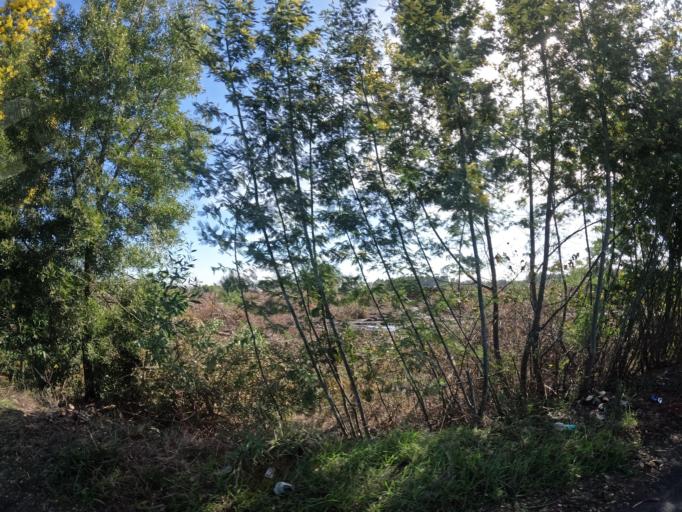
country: CL
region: Biobio
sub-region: Provincia de Biobio
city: Cabrero
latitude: -37.0401
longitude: -72.3746
